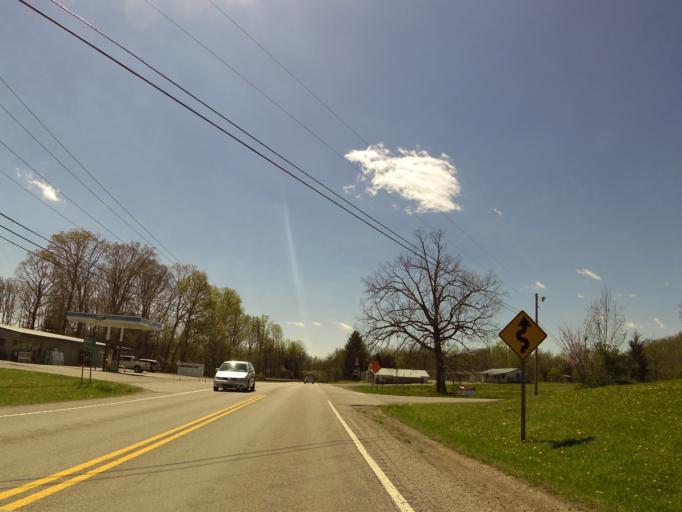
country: US
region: Tennessee
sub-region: DeKalb County
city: Smithville
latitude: 35.9754
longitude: -85.7036
